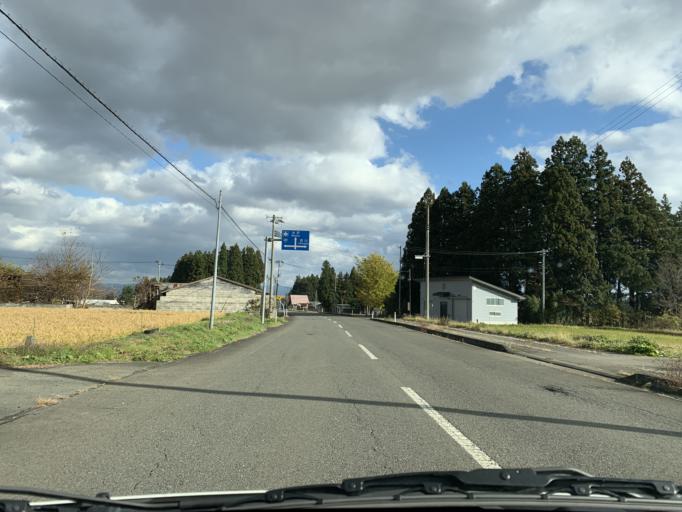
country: JP
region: Iwate
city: Mizusawa
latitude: 39.1143
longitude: 141.0112
